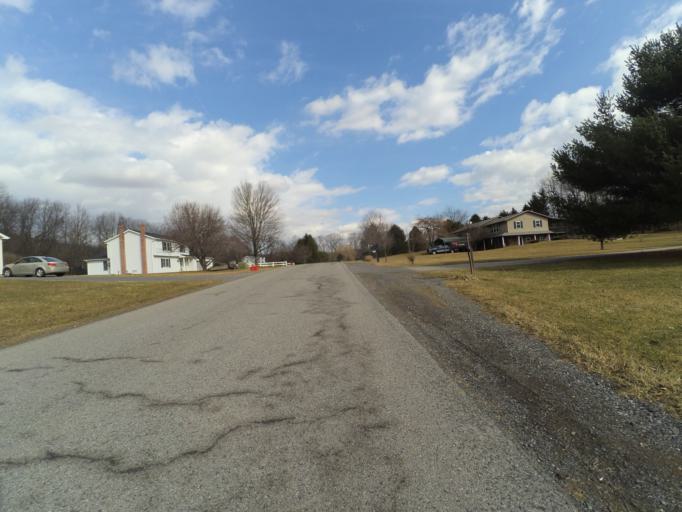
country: US
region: Pennsylvania
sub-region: Centre County
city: Stormstown
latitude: 40.7678
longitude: -78.0317
